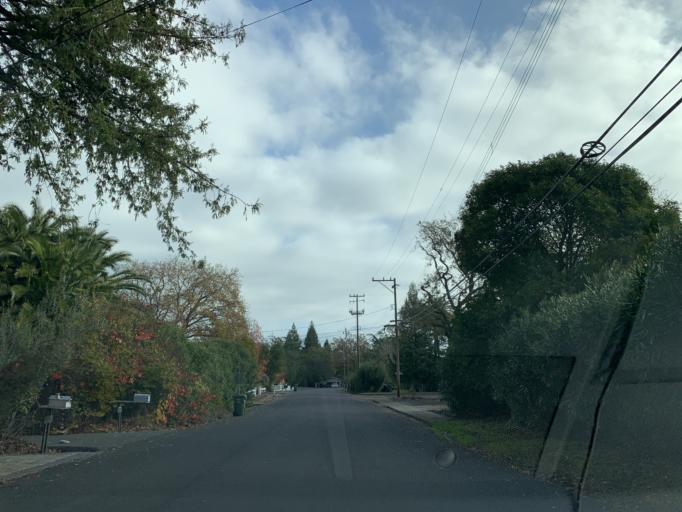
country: US
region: California
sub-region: Contra Costa County
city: Saranap
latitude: 37.8913
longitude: -122.0731
